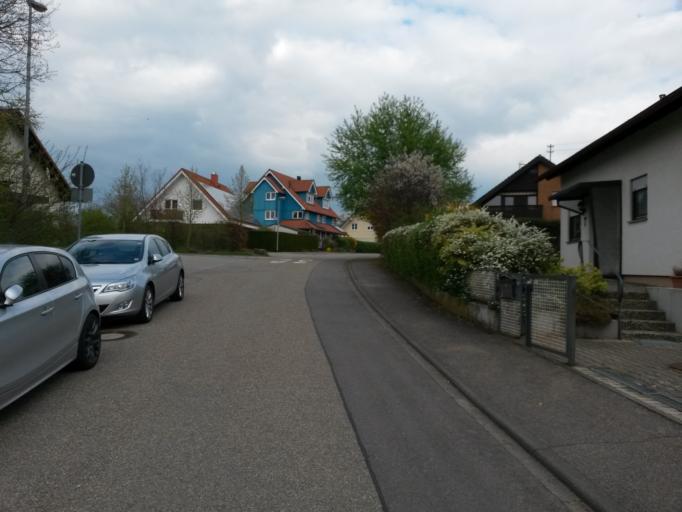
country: DE
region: Baden-Wuerttemberg
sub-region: Karlsruhe Region
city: Neuenburg
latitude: 48.8689
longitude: 8.5862
